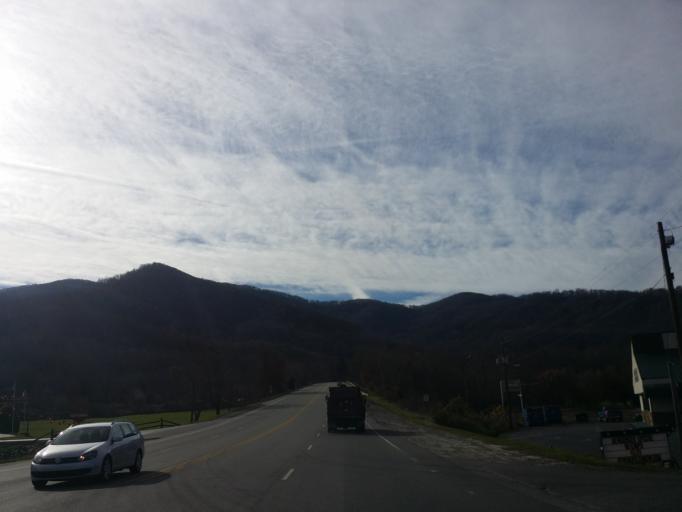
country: US
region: North Carolina
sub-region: Buncombe County
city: Swannanoa
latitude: 35.5994
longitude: -82.4033
